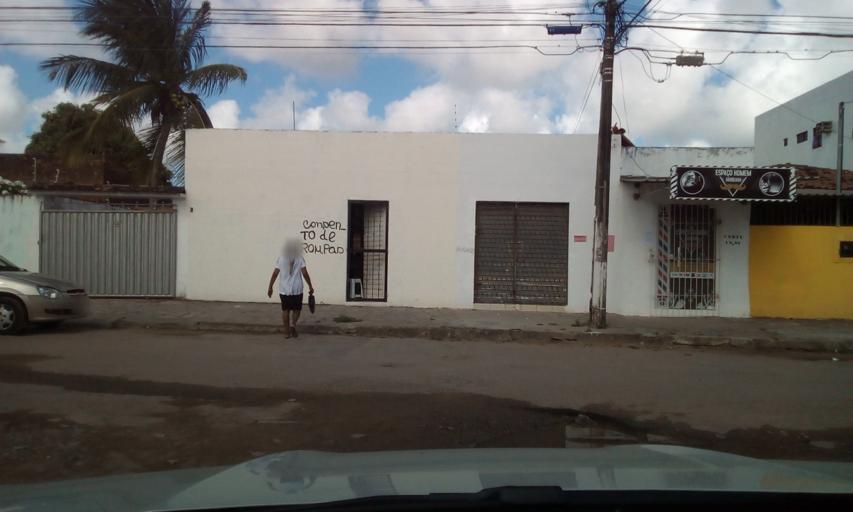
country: BR
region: Paraiba
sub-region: Joao Pessoa
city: Joao Pessoa
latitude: -7.1745
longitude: -34.8586
